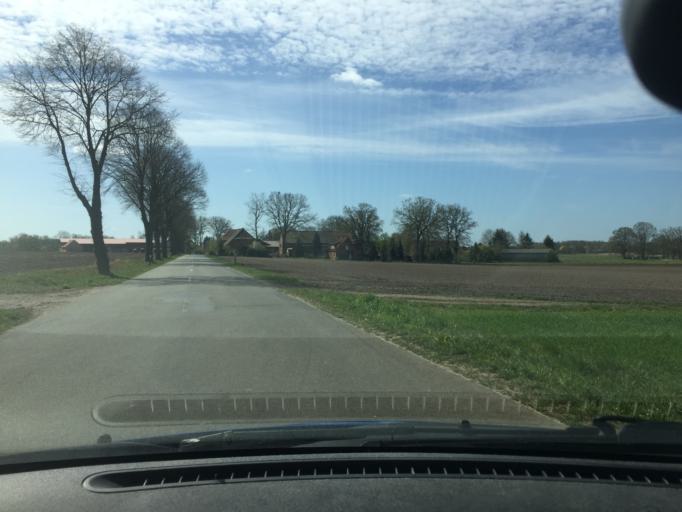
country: DE
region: Lower Saxony
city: Suhlendorf
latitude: 52.9274
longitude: 10.7127
